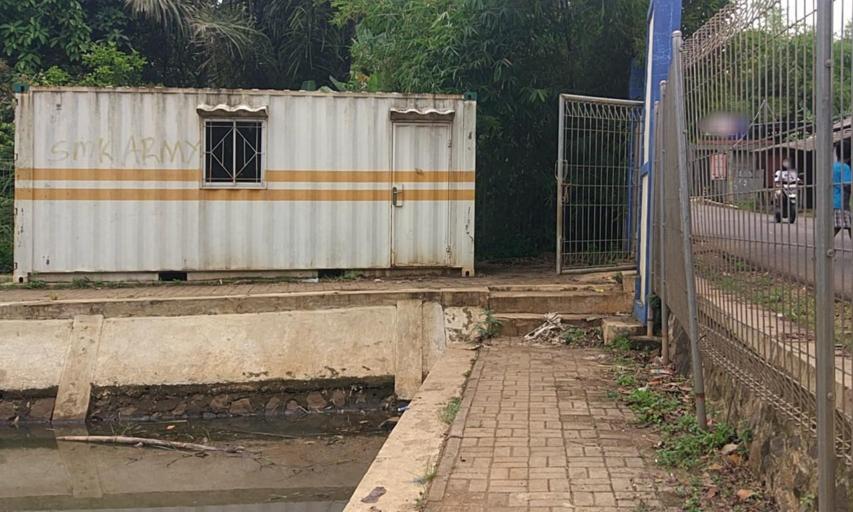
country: ID
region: West Java
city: Parung
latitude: -6.4731
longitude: 106.7764
